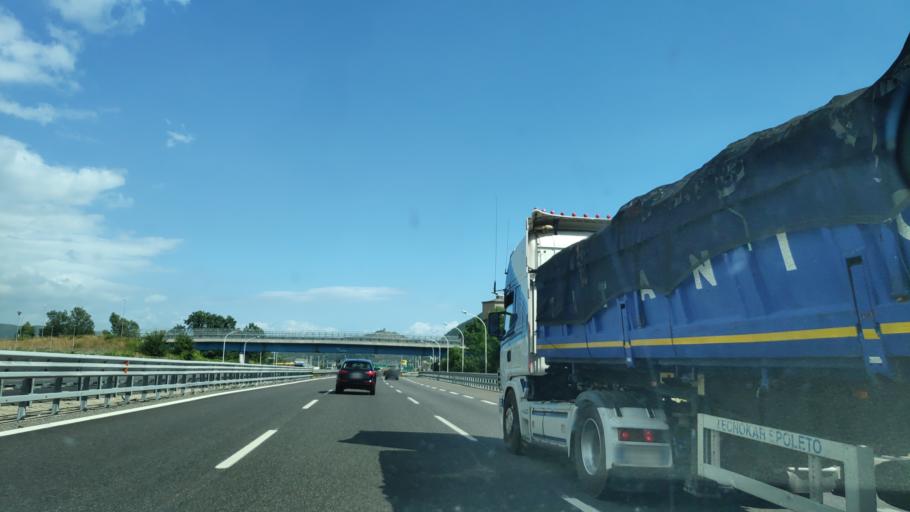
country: IT
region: Campania
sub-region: Provincia di Salerno
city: San Mango Piemonte
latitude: 40.6948
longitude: 14.8316
